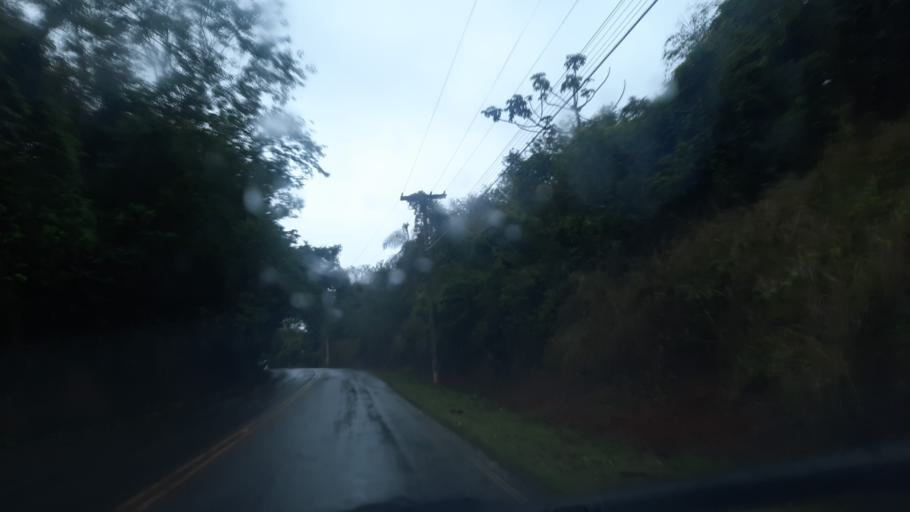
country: BR
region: Sao Paulo
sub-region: Atibaia
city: Atibaia
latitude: -23.0780
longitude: -46.5229
